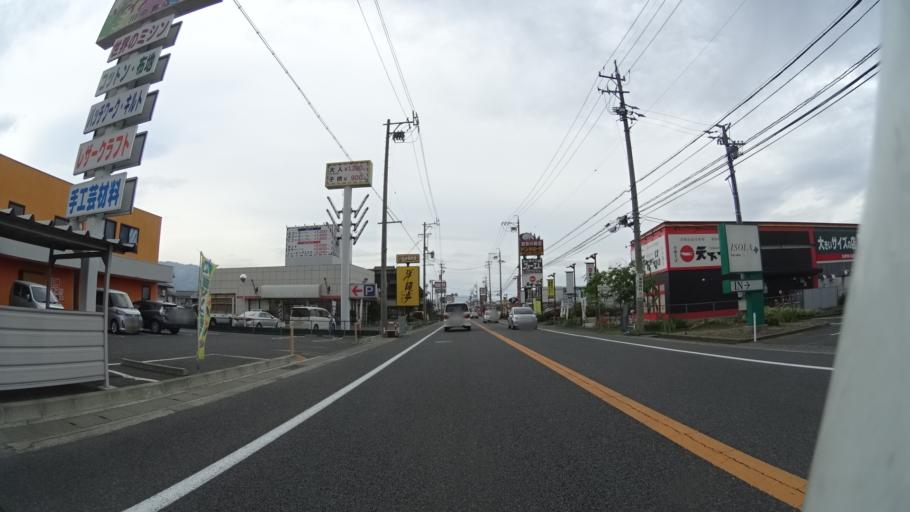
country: JP
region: Nagano
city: Nagano-shi
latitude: 36.5964
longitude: 138.1574
